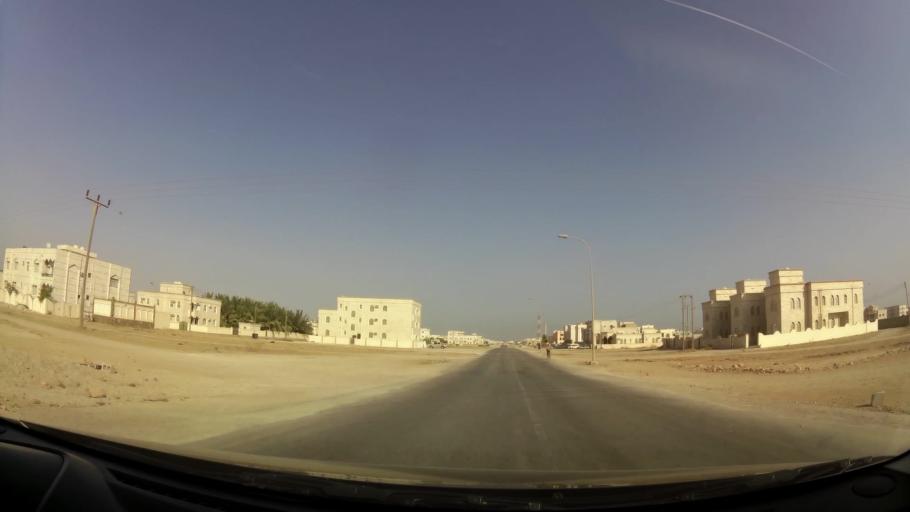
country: OM
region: Zufar
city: Salalah
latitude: 17.0218
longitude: 54.0168
